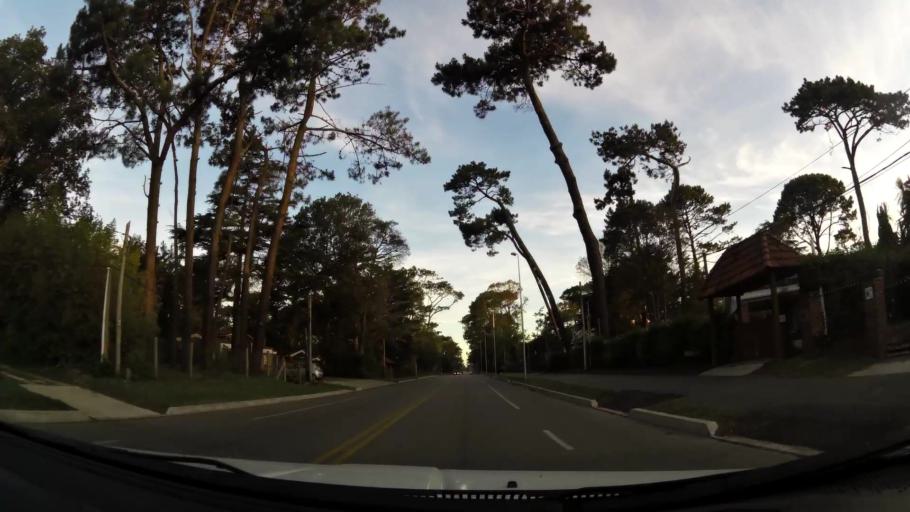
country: UY
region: Maldonado
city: Maldonado
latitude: -34.9168
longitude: -54.9507
